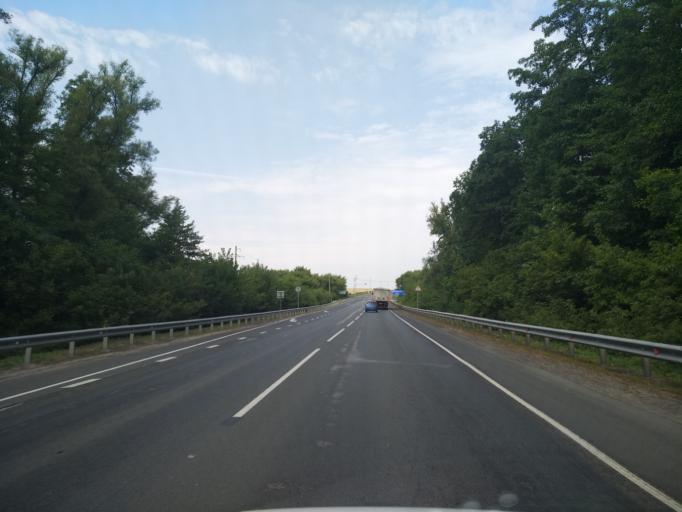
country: RU
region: Voronezj
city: Orlovo
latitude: 51.6816
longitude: 39.5764
